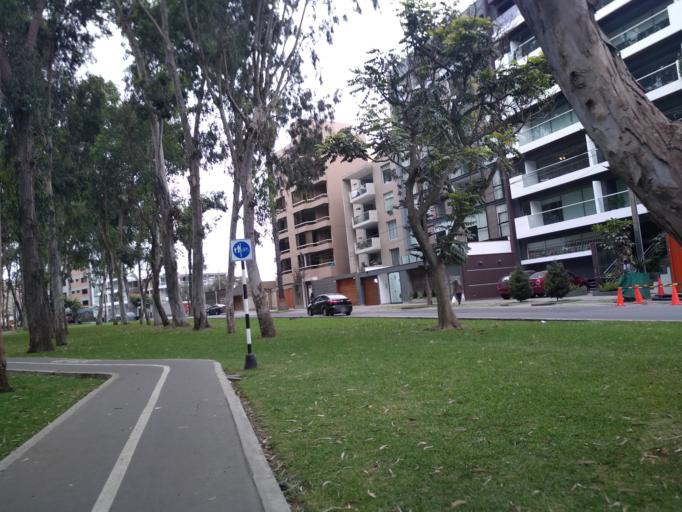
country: PE
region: Lima
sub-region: Lima
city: San Luis
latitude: -12.1042
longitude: -77.0130
